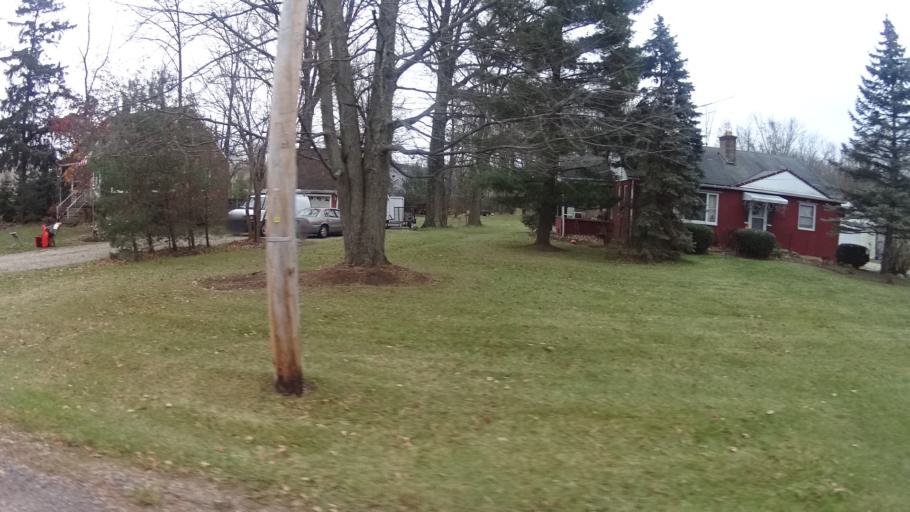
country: US
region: Ohio
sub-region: Lorain County
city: North Ridgeville
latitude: 41.3712
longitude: -81.9787
